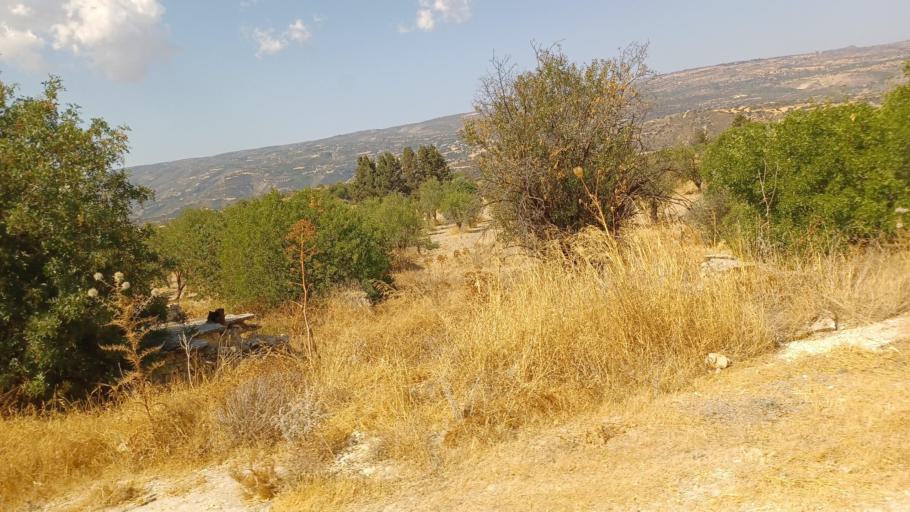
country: CY
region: Pafos
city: Polis
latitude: 34.9742
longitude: 32.4889
